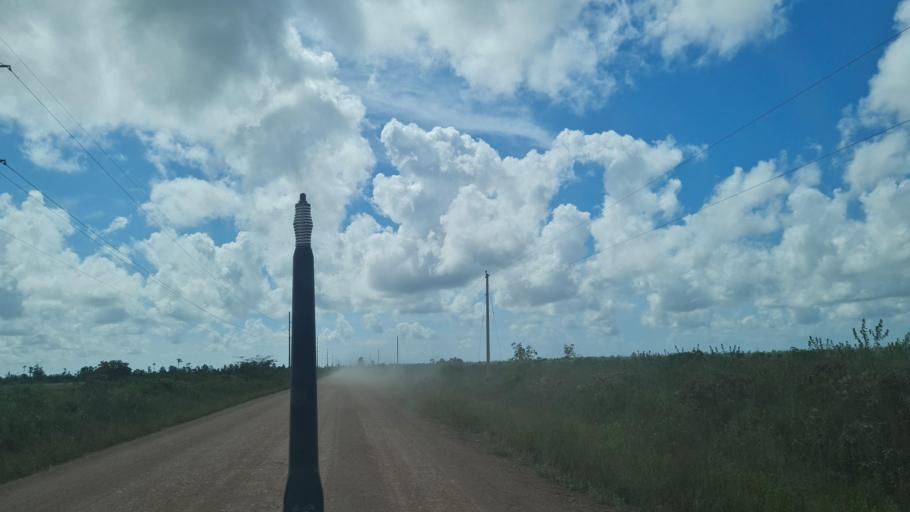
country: NI
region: Atlantico Norte (RAAN)
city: Puerto Cabezas
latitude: 14.1090
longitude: -83.5802
